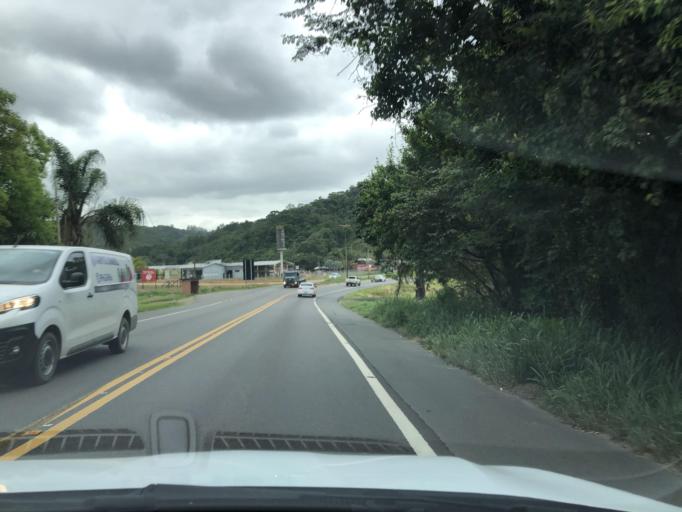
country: BR
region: Santa Catarina
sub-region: Ibirama
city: Ibirama
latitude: -27.0846
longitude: -49.5201
